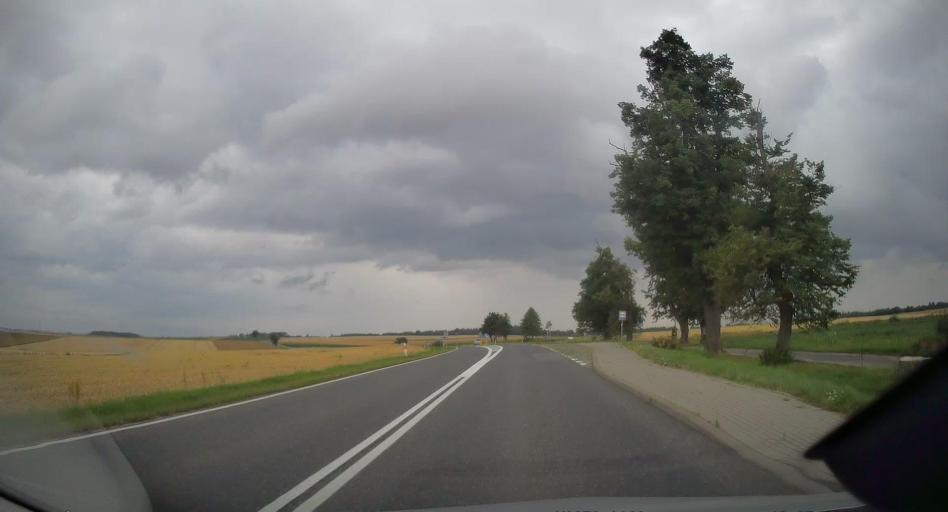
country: PL
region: Opole Voivodeship
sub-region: Powiat prudnicki
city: Laka Prudnicka
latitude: 50.4183
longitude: 17.4831
